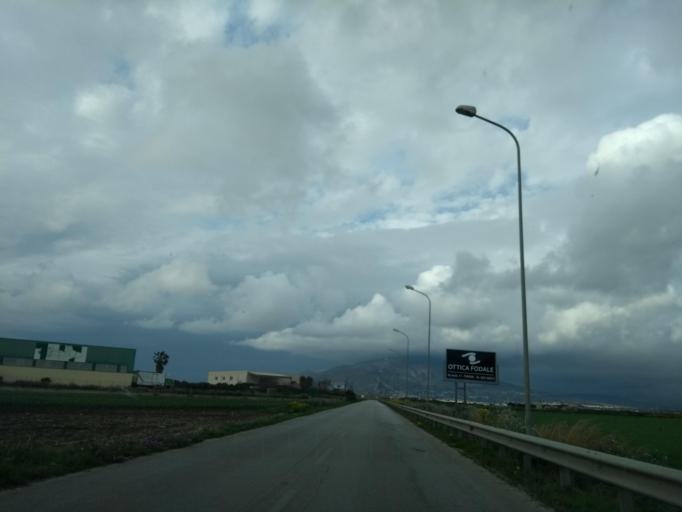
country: IT
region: Sicily
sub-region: Trapani
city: Paceco
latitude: 37.9733
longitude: 12.5254
